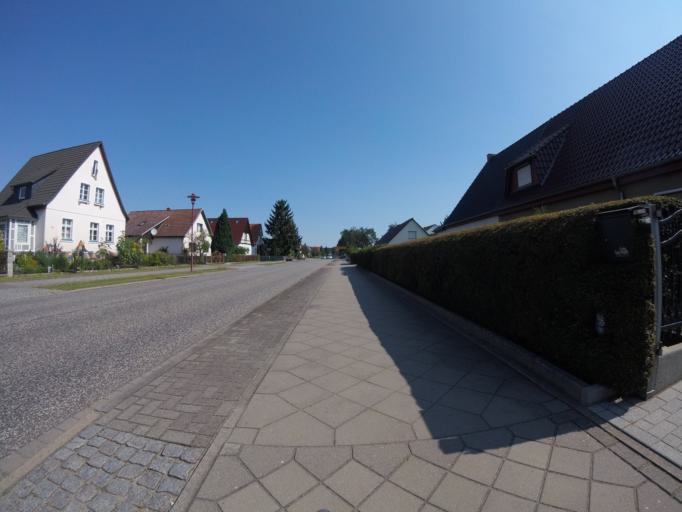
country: DE
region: Brandenburg
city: Mullrose
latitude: 52.2542
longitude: 14.4230
